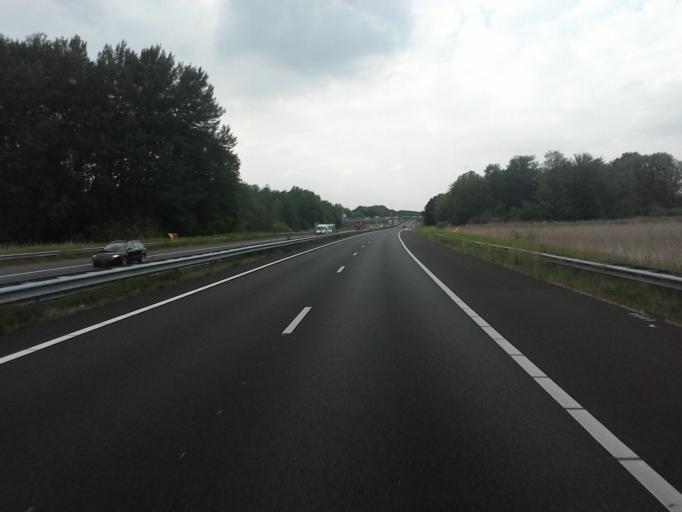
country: NL
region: Limburg
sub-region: Gemeente Venray
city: Venray
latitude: 51.5178
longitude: 6.0048
